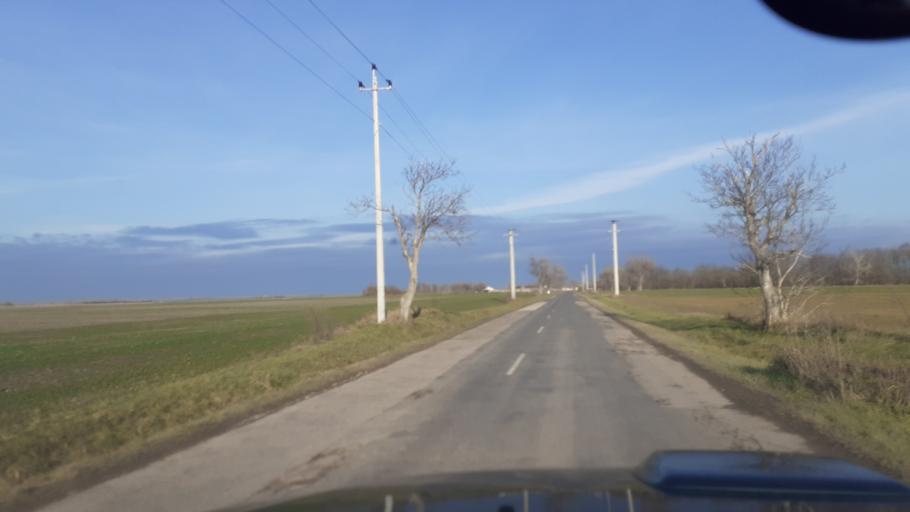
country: HU
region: Pest
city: Domsod
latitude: 47.1052
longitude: 19.0513
